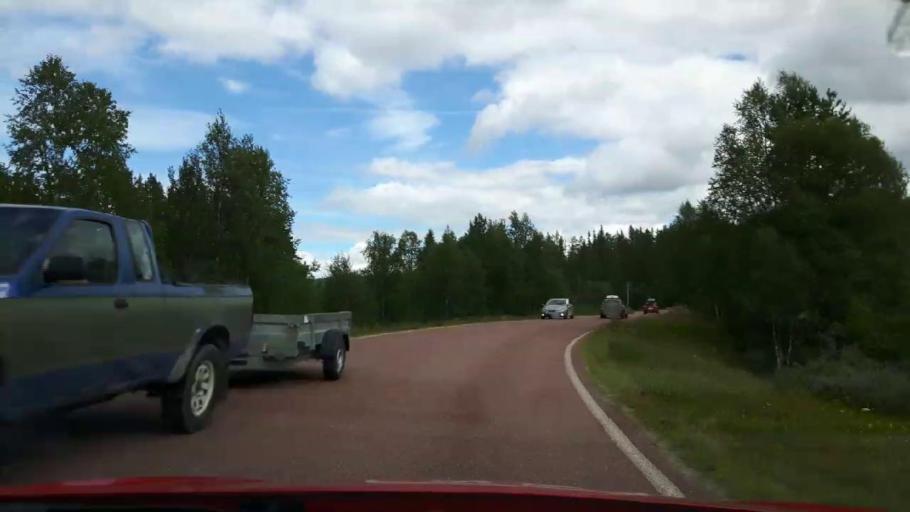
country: NO
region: Hedmark
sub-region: Trysil
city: Innbygda
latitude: 61.9938
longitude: 12.9793
